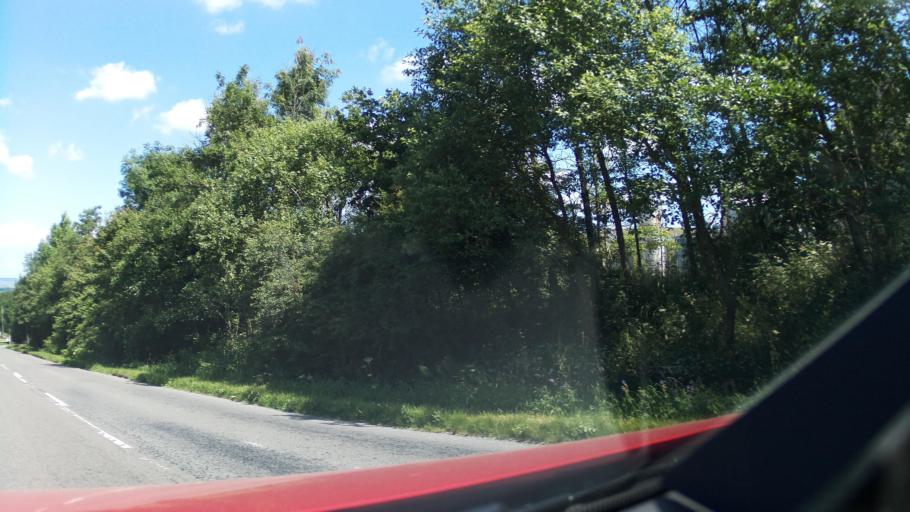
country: GB
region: England
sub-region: Derbyshire
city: Buxton
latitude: 53.2177
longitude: -1.8725
